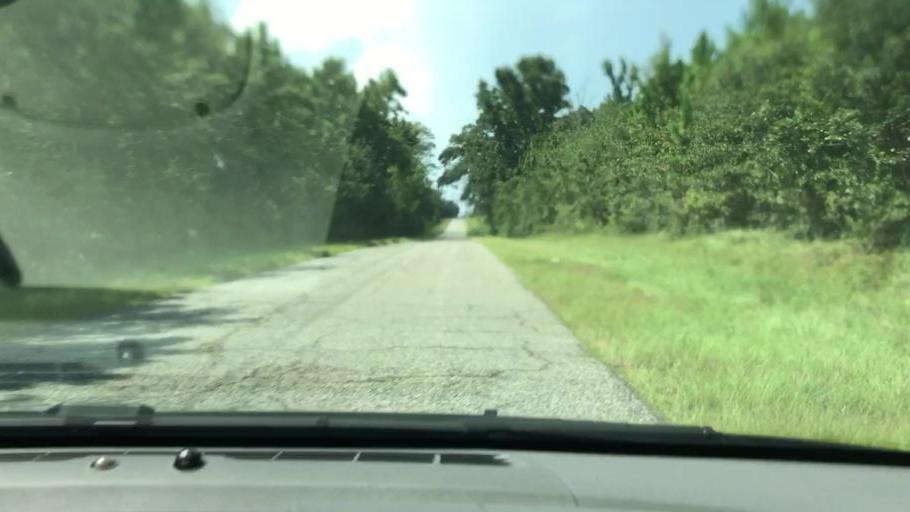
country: US
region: Georgia
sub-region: Seminole County
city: Donalsonville
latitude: 31.1624
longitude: -84.9983
